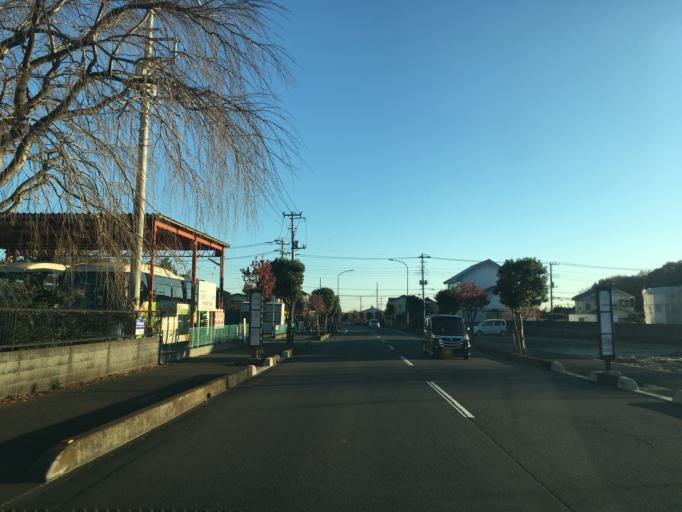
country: JP
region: Saitama
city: Sayama
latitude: 35.8130
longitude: 139.4007
